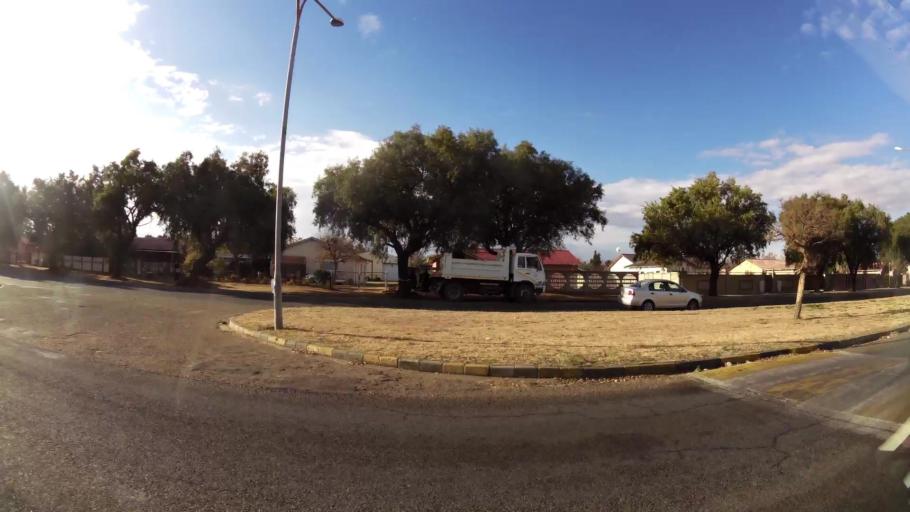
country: ZA
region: Orange Free State
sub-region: Lejweleputswa District Municipality
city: Welkom
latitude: -27.9880
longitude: 26.7410
